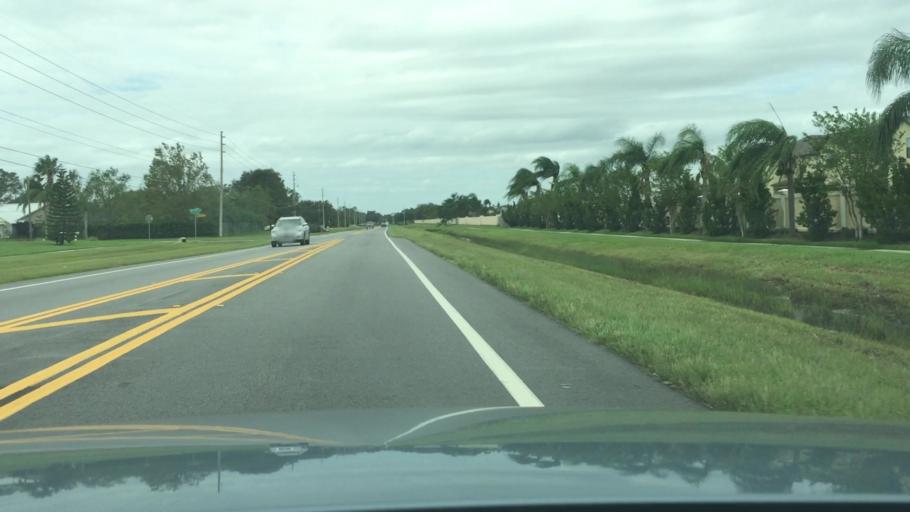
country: US
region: Florida
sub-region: Osceola County
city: Saint Cloud
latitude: 28.2025
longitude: -81.2982
